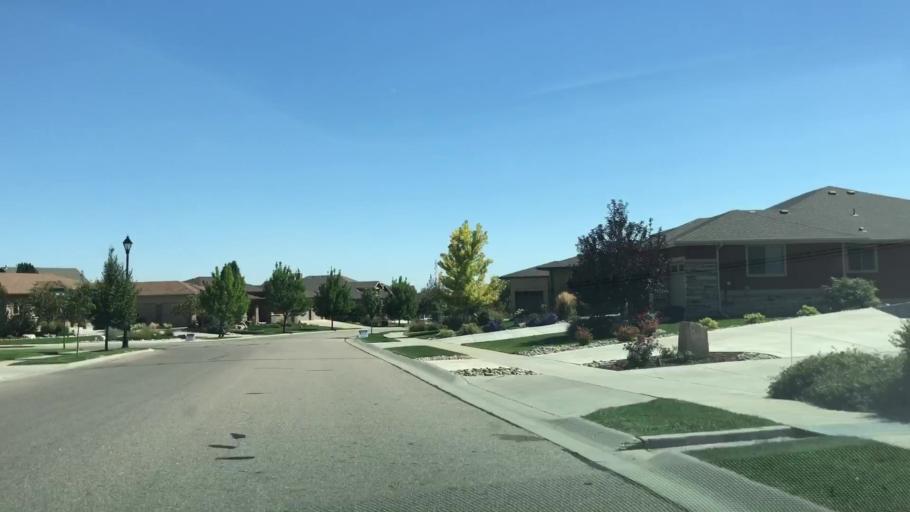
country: US
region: Colorado
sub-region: Larimer County
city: Loveland
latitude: 40.3992
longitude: -104.9818
